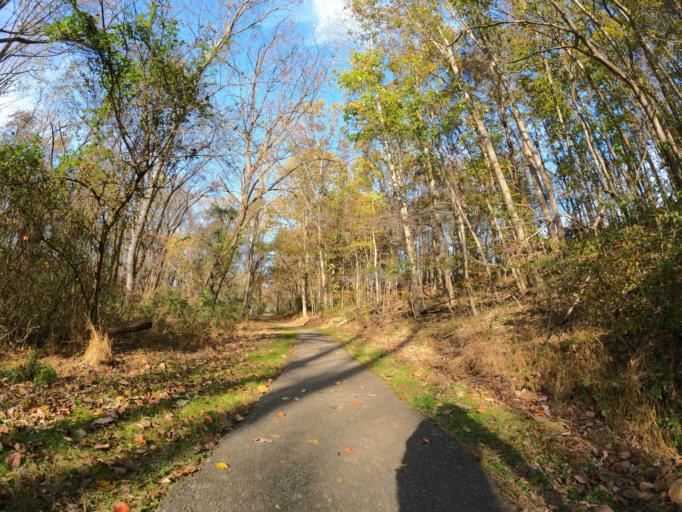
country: US
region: Maryland
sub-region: Carroll County
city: Sykesville
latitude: 39.3717
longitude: -76.9809
